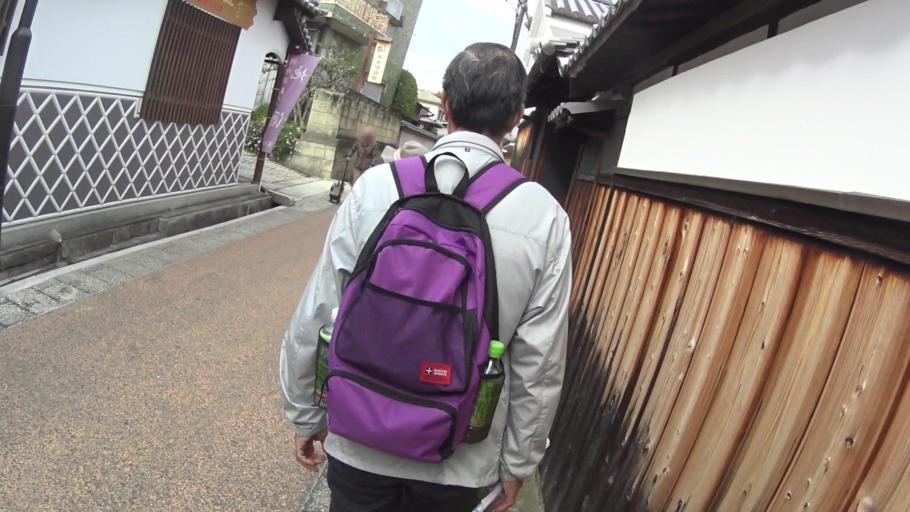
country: JP
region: Osaka
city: Kashihara
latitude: 34.5682
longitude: 135.5967
